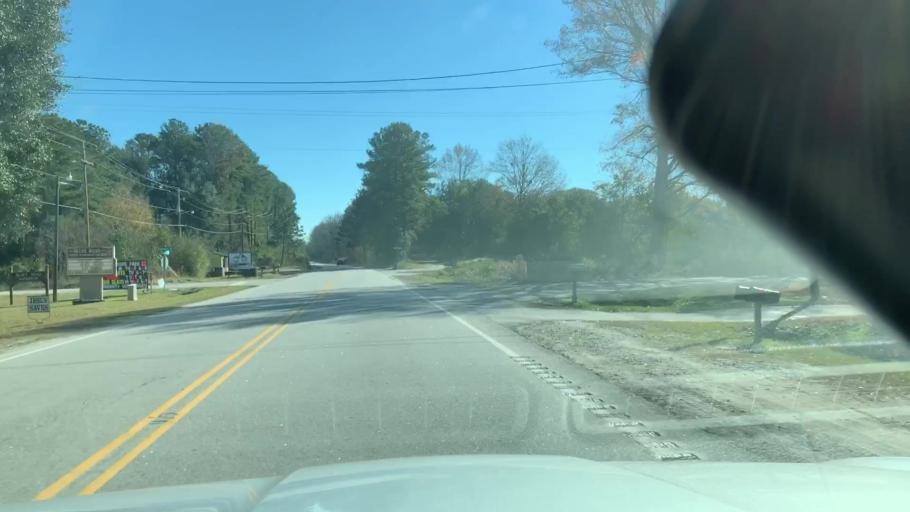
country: US
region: South Carolina
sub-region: Richland County
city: Hopkins
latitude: 33.9264
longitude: -80.9621
